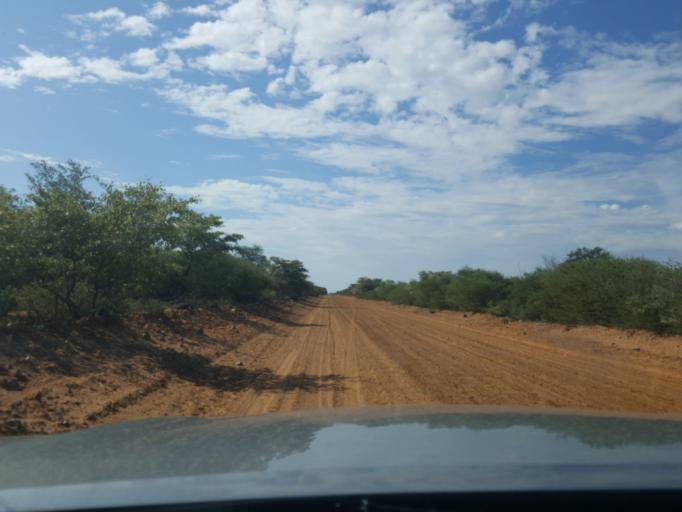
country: BW
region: Kweneng
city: Khudumelapye
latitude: -23.6307
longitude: 24.7285
